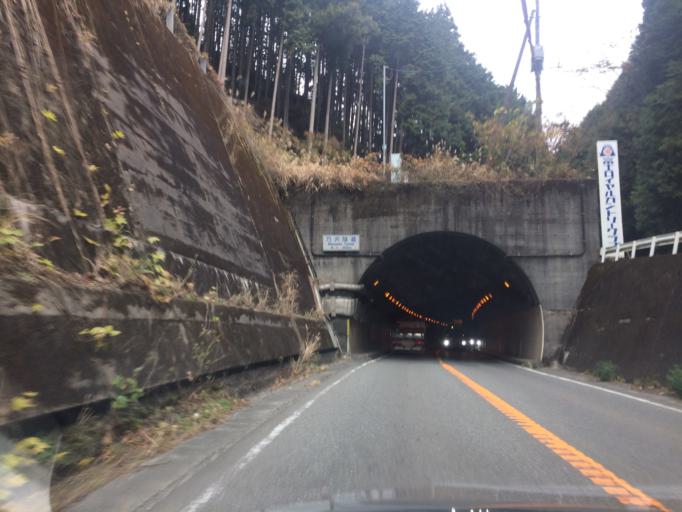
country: JP
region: Shizuoka
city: Fujinomiya
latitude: 35.2062
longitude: 138.5158
